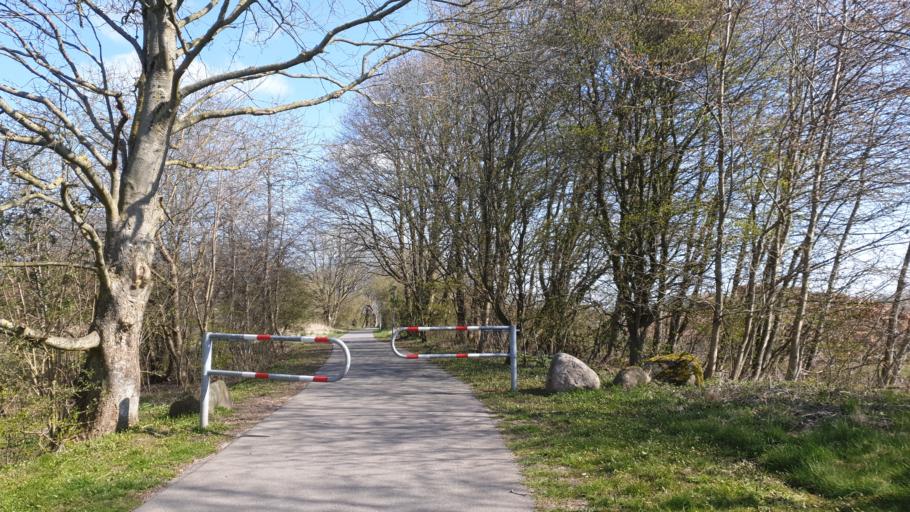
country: DK
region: Central Jutland
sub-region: Hedensted Kommune
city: Hedensted
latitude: 55.8065
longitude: 9.7021
